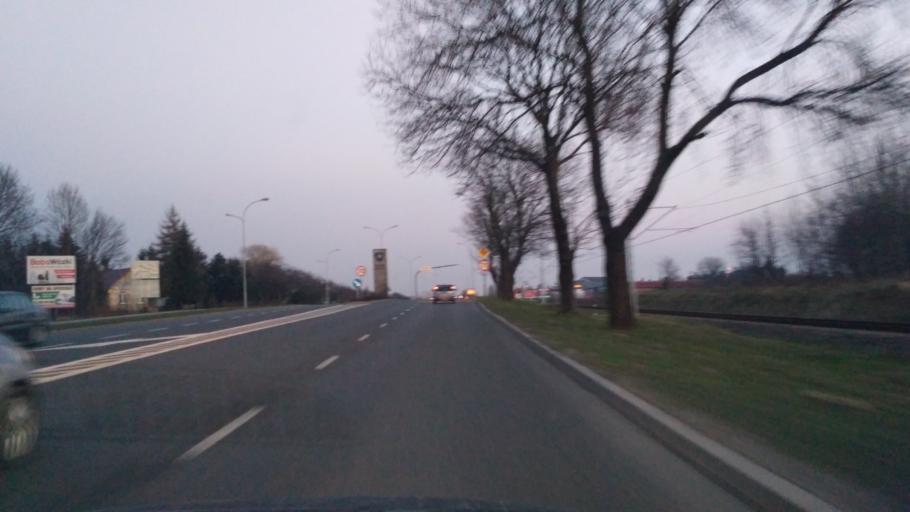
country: PL
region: Subcarpathian Voivodeship
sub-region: Rzeszow
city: Rzeszow
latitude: 50.0735
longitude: 21.9883
